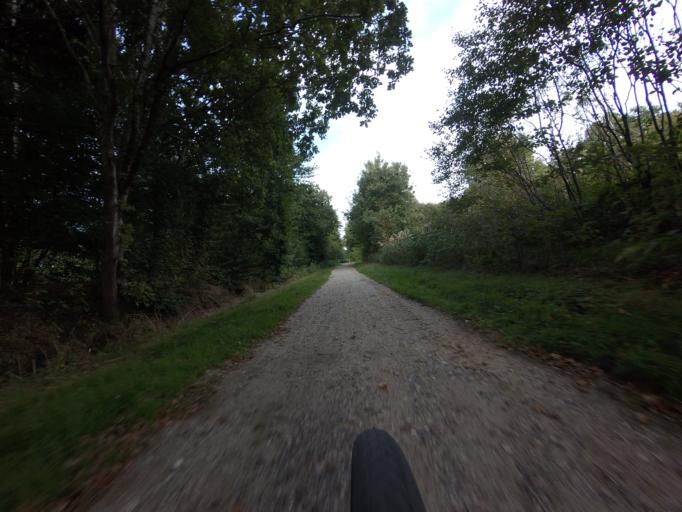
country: DK
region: Central Jutland
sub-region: Ikast-Brande Kommune
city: Brande
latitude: 55.9178
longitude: 9.1032
